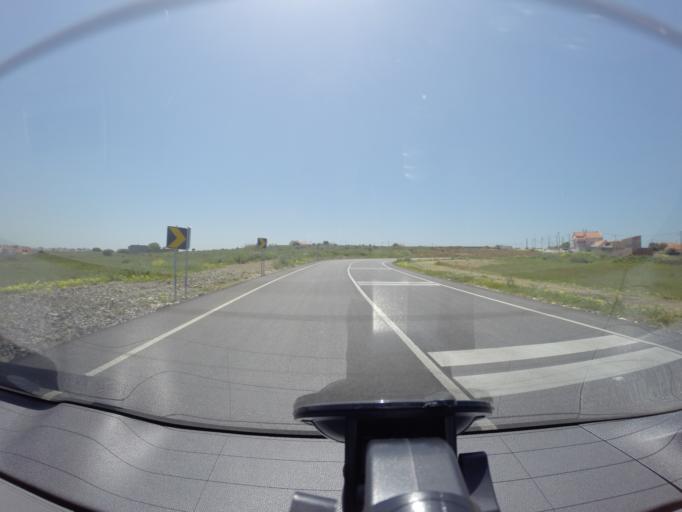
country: PT
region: Lisbon
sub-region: Cascais
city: Parede
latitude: 38.7188
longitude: -9.3575
